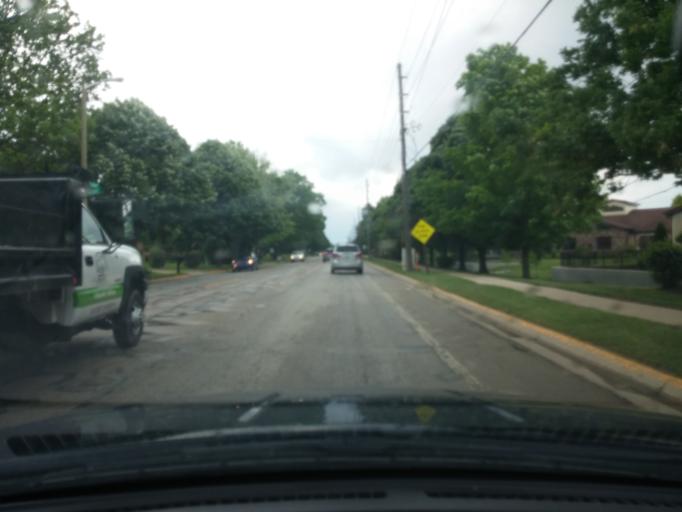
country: US
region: Indiana
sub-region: Tippecanoe County
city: West Lafayette
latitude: 40.4582
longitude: -86.9157
